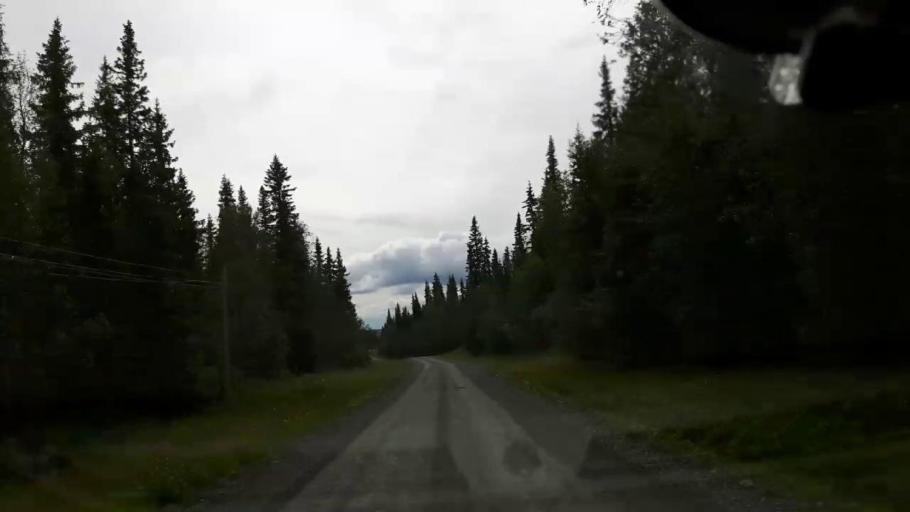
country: SE
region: Jaemtland
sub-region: Krokoms Kommun
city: Valla
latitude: 63.7140
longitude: 13.8605
